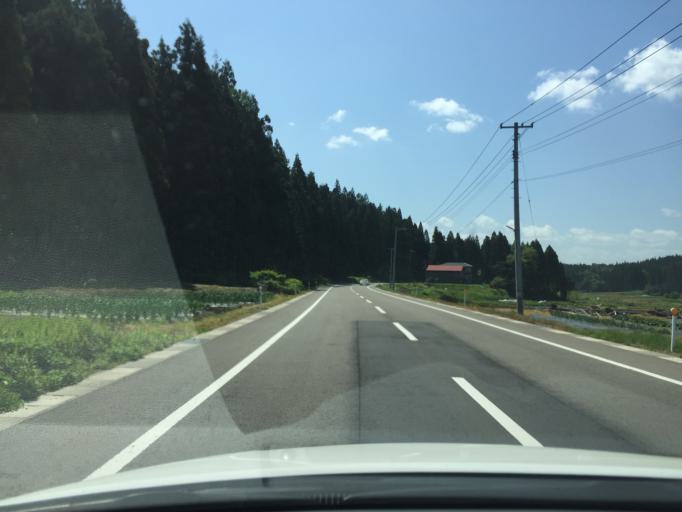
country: JP
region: Niigata
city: Kamo
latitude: 37.5691
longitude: 139.0841
